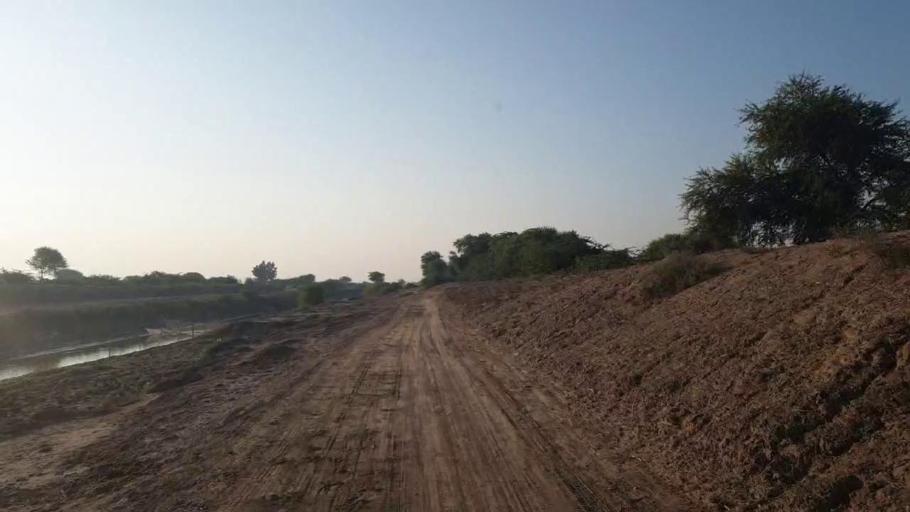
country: PK
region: Sindh
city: Badin
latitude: 24.6465
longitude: 68.7901
